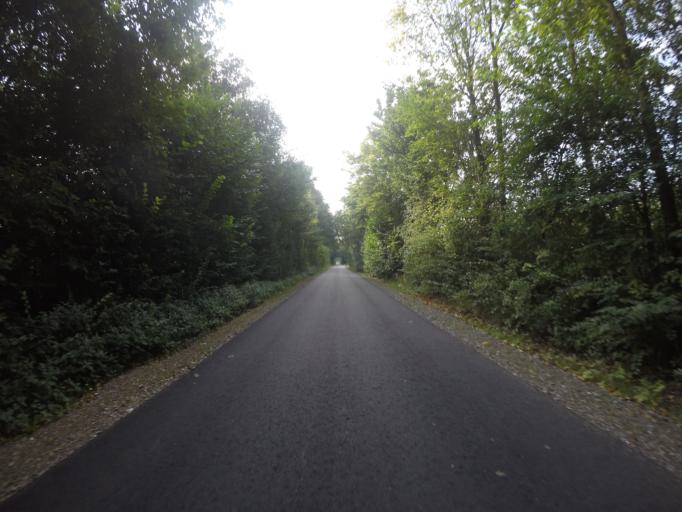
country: DE
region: North Rhine-Westphalia
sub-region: Regierungsbezirk Dusseldorf
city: Bocholt
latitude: 51.8303
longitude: 6.5519
